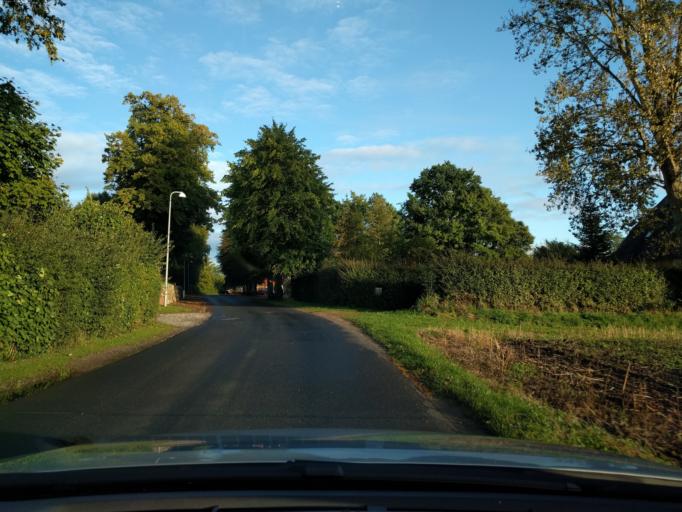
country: DK
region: South Denmark
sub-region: Odense Kommune
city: Bullerup
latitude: 55.4279
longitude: 10.4908
